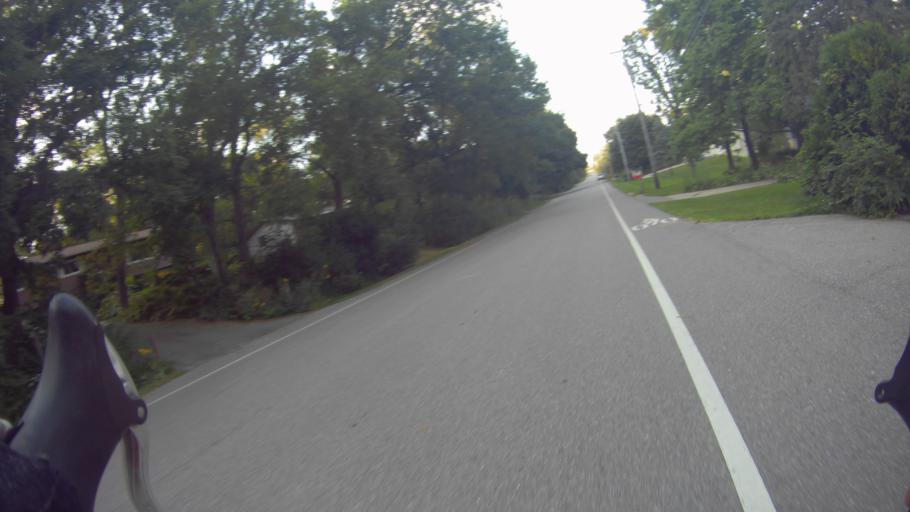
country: US
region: Wisconsin
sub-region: Dane County
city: Madison
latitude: 43.0119
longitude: -89.4259
